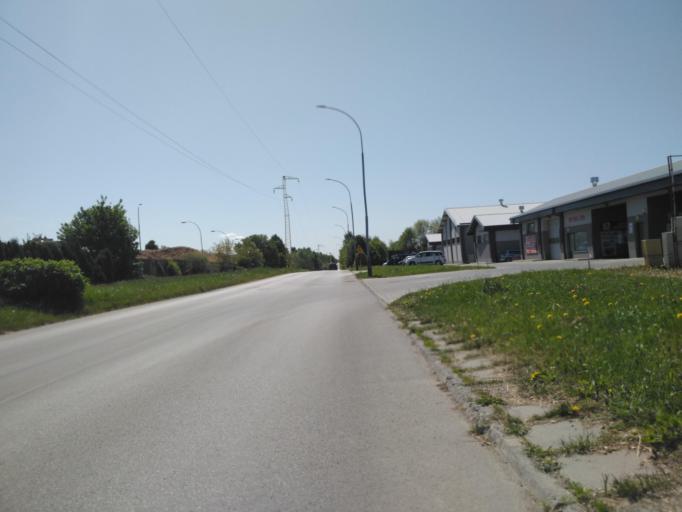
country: PL
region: Subcarpathian Voivodeship
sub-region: Krosno
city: Krosno
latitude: 49.6794
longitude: 21.7814
